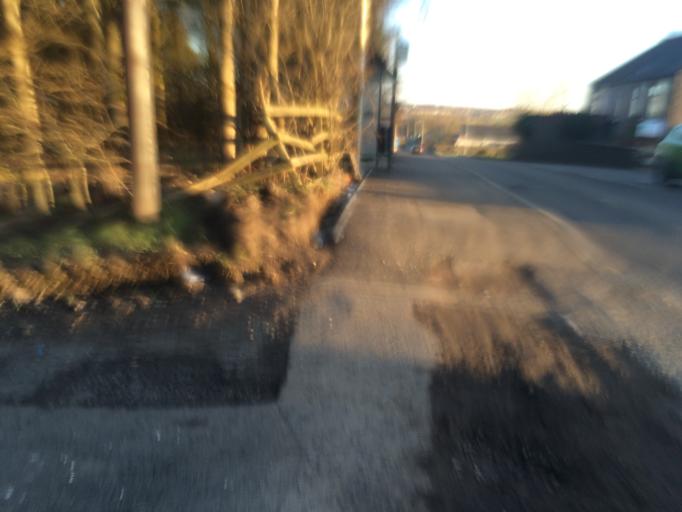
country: GB
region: Scotland
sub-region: Fife
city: Ballingry
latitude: 56.1472
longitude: -3.3249
